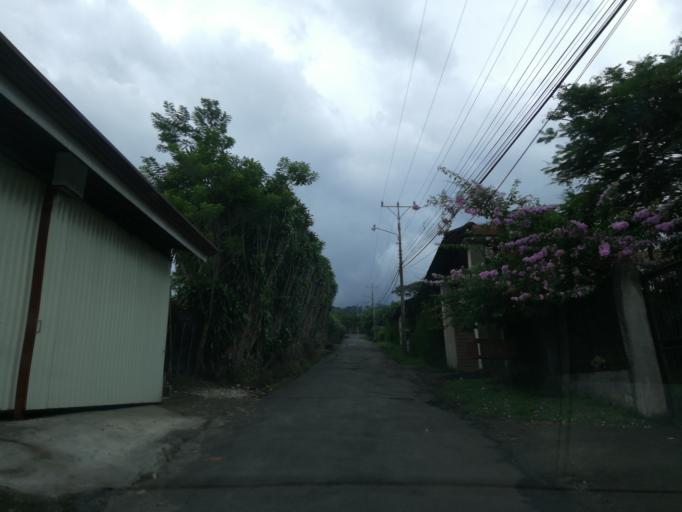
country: CR
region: Heredia
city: Santo Domingo
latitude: 10.0384
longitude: -84.1814
